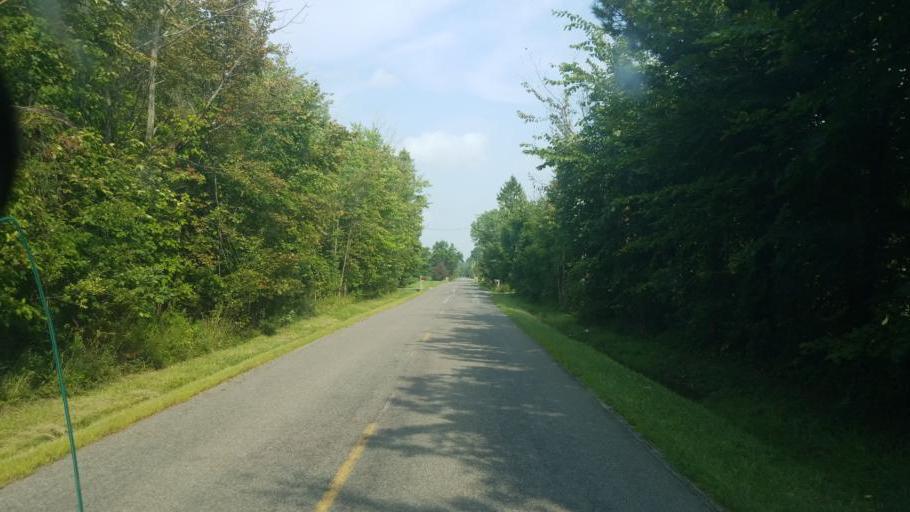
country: US
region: Ohio
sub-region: Medina County
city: Medina
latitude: 41.1578
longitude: -81.9876
